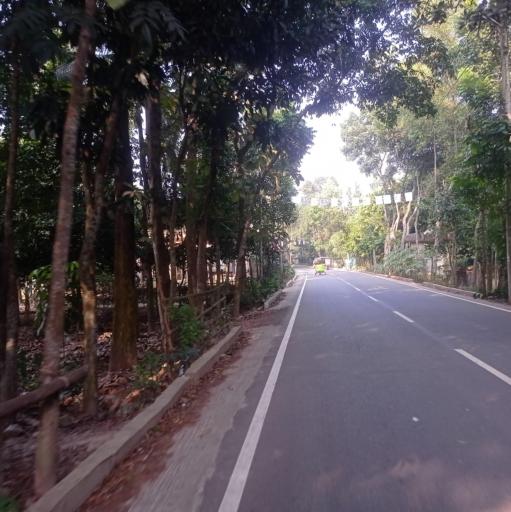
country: BD
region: Dhaka
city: Bhairab Bazar
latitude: 24.0485
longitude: 90.8353
